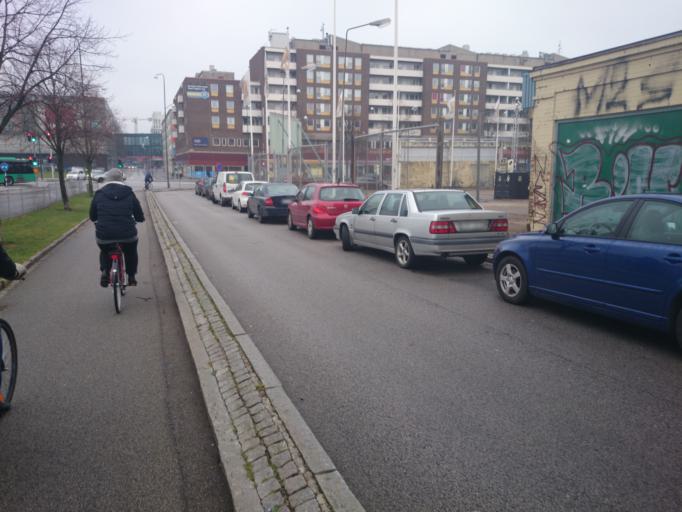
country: SE
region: Skane
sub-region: Malmo
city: Malmoe
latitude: 55.6083
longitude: 13.0202
